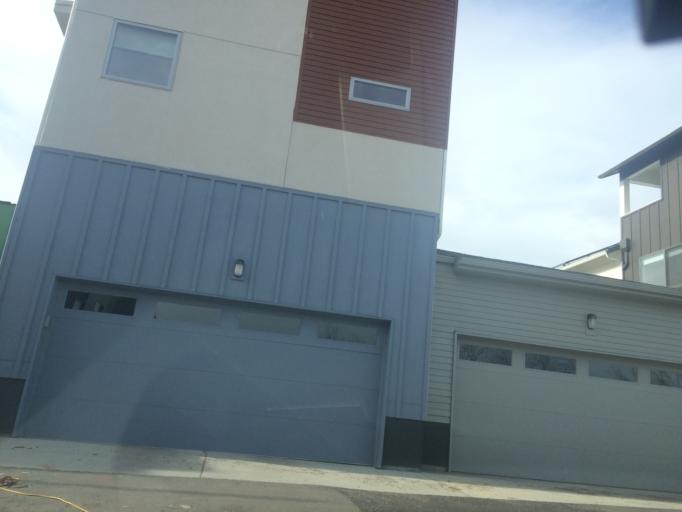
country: US
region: Colorado
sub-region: Jefferson County
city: Applewood
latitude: 39.8225
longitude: -105.1700
